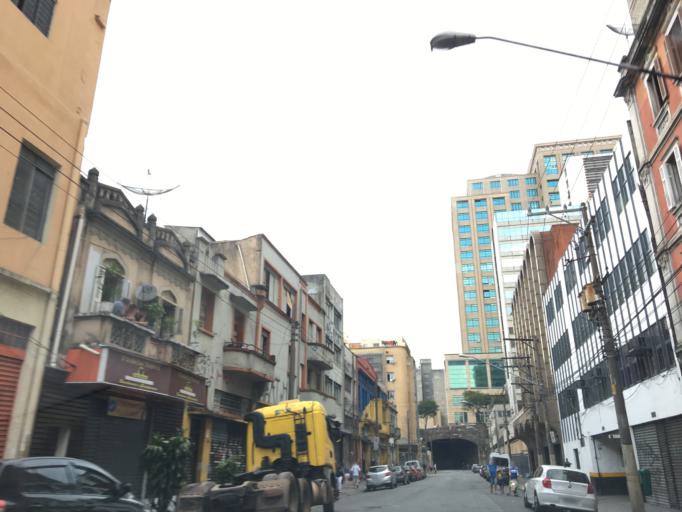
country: BR
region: Sao Paulo
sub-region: Sao Paulo
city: Sao Paulo
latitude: -23.5481
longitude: -46.6309
